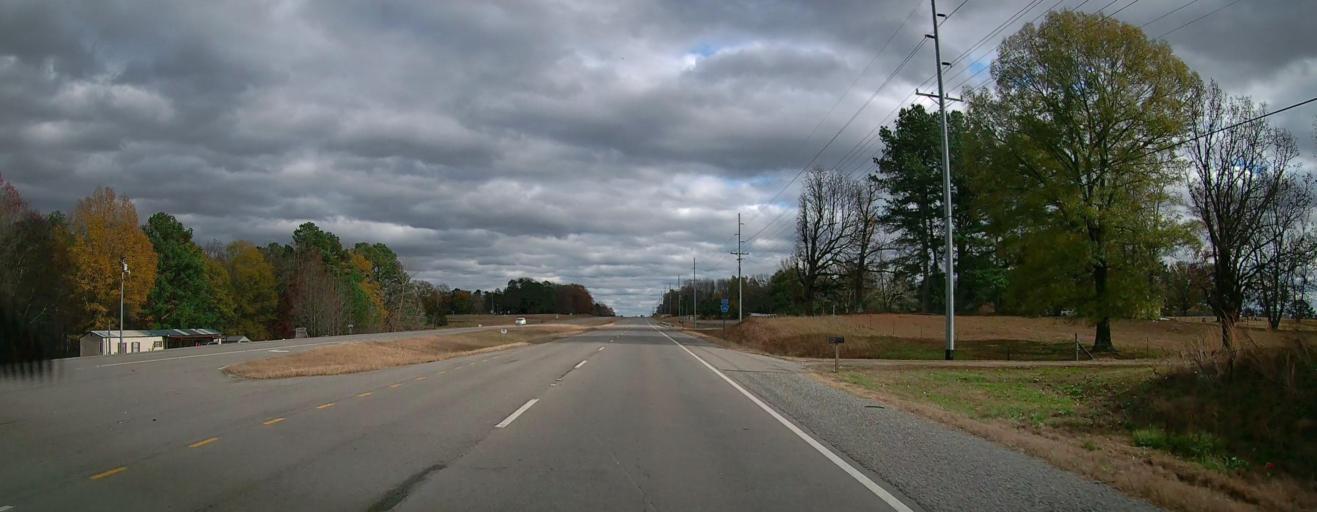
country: US
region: Alabama
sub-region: Lawrence County
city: Town Creek
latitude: 34.5712
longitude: -87.3878
